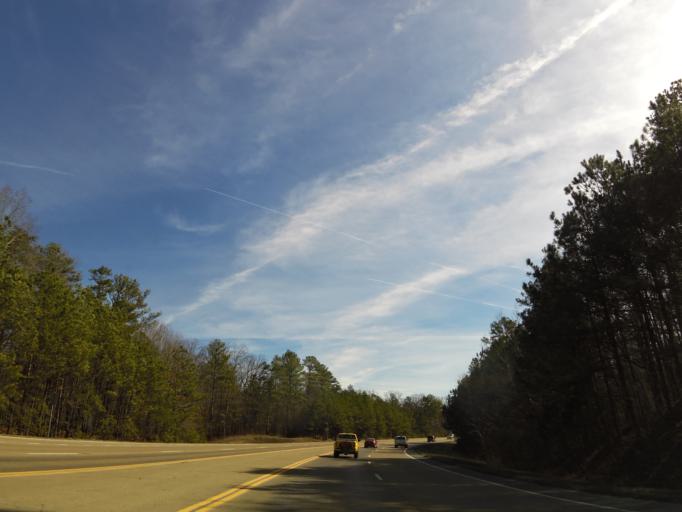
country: US
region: Georgia
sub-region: Whitfield County
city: Dalton
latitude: 34.7879
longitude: -84.9232
